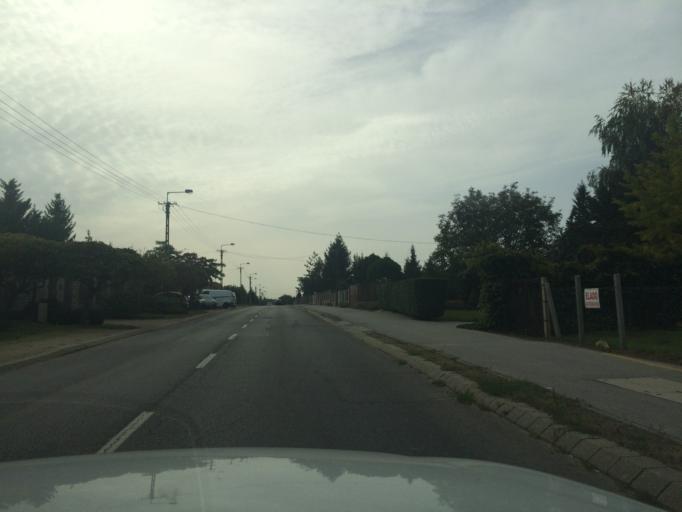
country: HU
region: Szabolcs-Szatmar-Bereg
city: Nyiregyhaza
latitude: 47.9921
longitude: 21.7303
